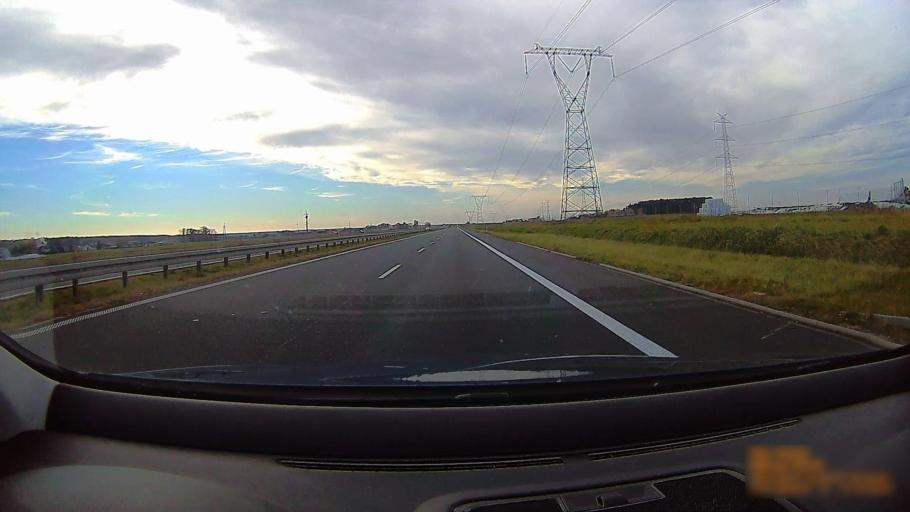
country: PL
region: Greater Poland Voivodeship
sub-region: Powiat ostrowski
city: Przygodzice
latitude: 51.6136
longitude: 17.8583
